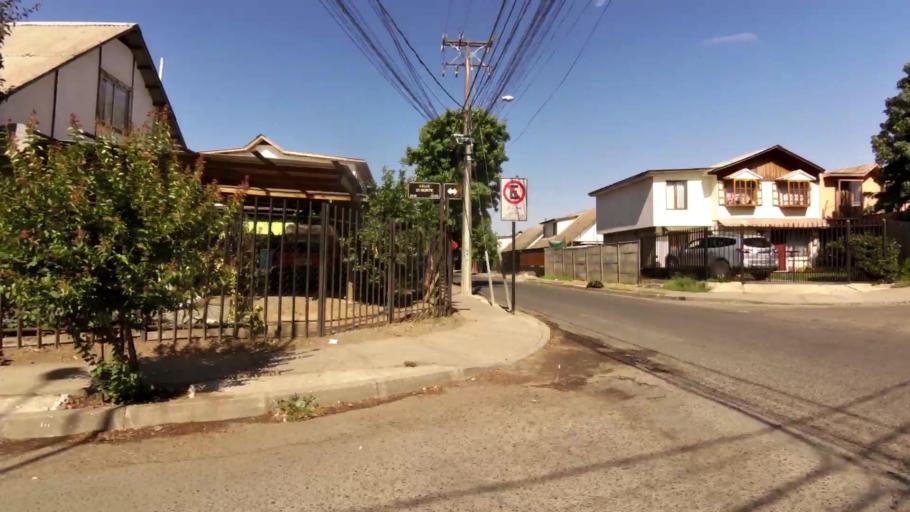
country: CL
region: Maule
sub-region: Provincia de Talca
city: Talca
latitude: -35.4099
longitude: -71.6381
